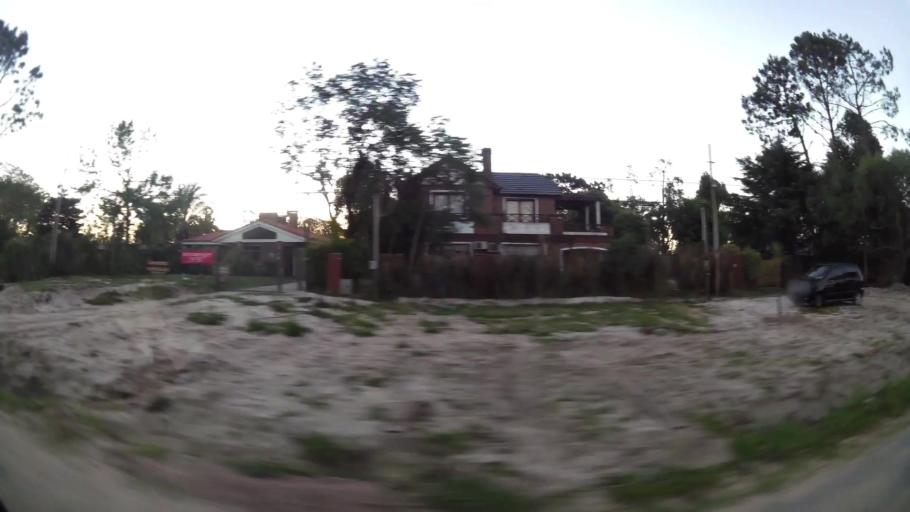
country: UY
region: Canelones
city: Colonia Nicolich
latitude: -34.8258
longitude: -55.9565
